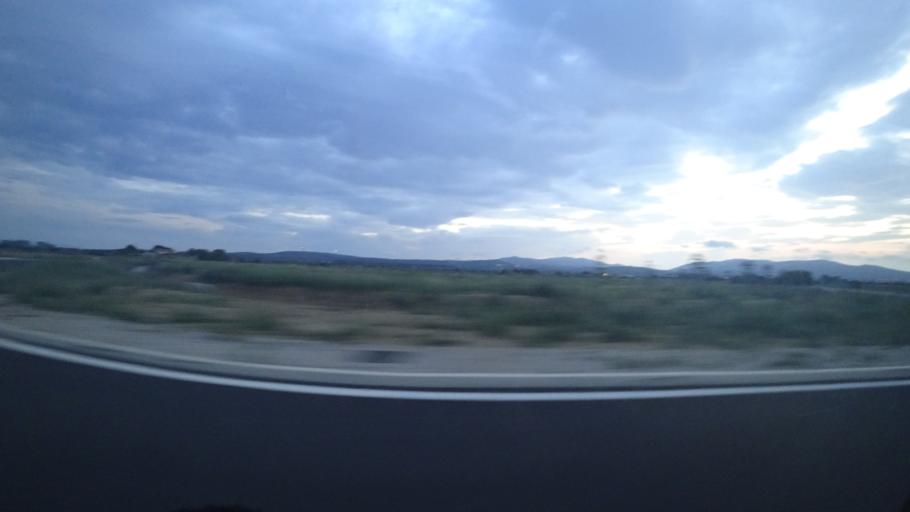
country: FR
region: Languedoc-Roussillon
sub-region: Departement de l'Aude
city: Leucate
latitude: 42.9336
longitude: 3.0027
